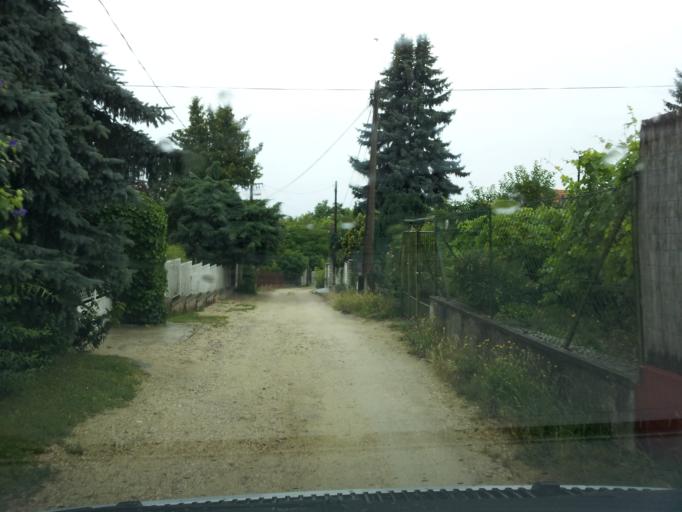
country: HU
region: Veszprem
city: Balatonkenese
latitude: 47.0238
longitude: 18.1417
